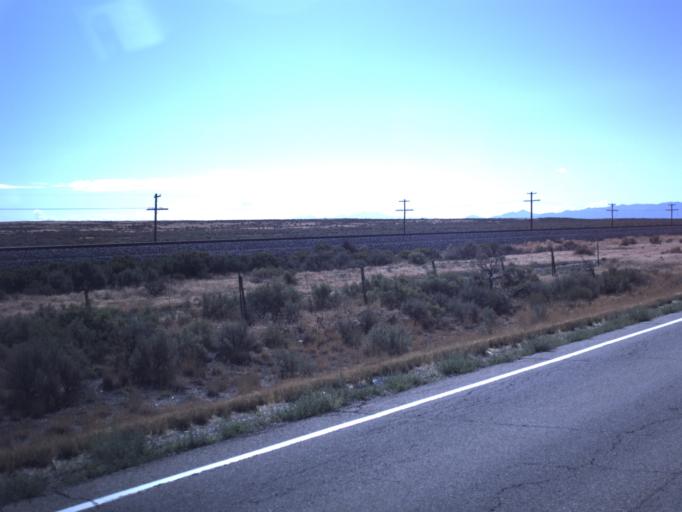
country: US
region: Utah
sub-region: Tooele County
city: Tooele
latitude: 40.3442
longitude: -112.4110
